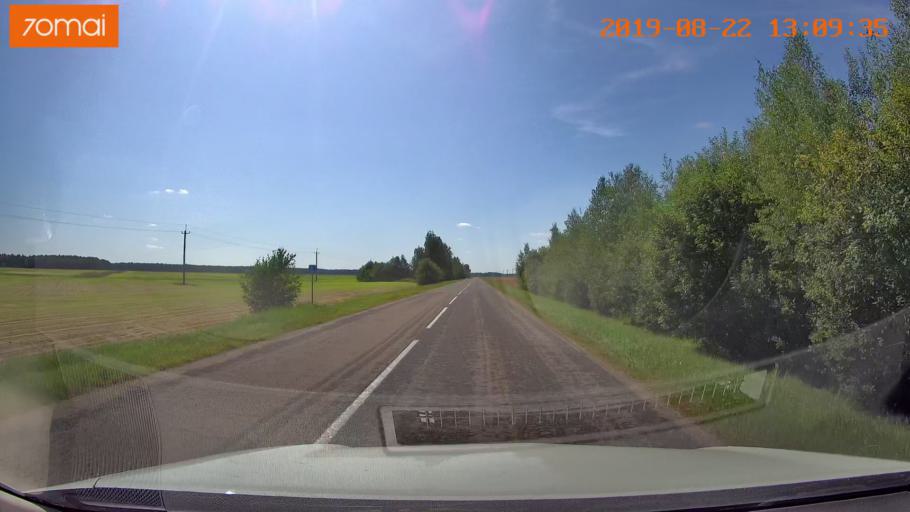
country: BY
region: Minsk
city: Prawdzinski
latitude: 53.3083
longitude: 27.8504
